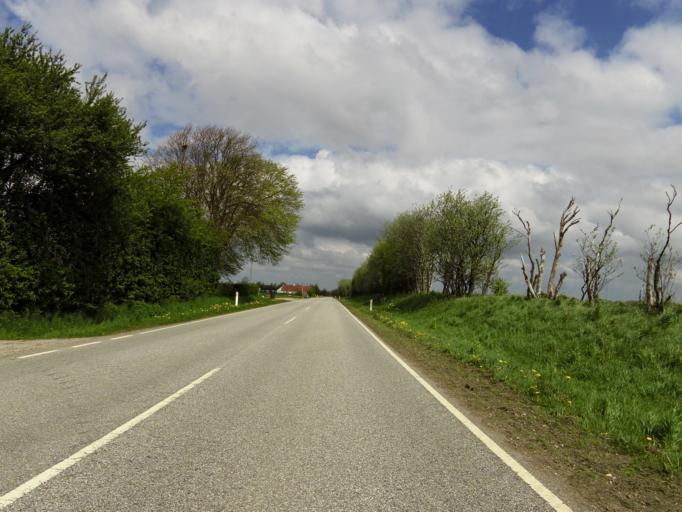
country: DK
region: South Denmark
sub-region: Haderslev Kommune
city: Gram
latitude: 55.2337
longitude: 8.9618
